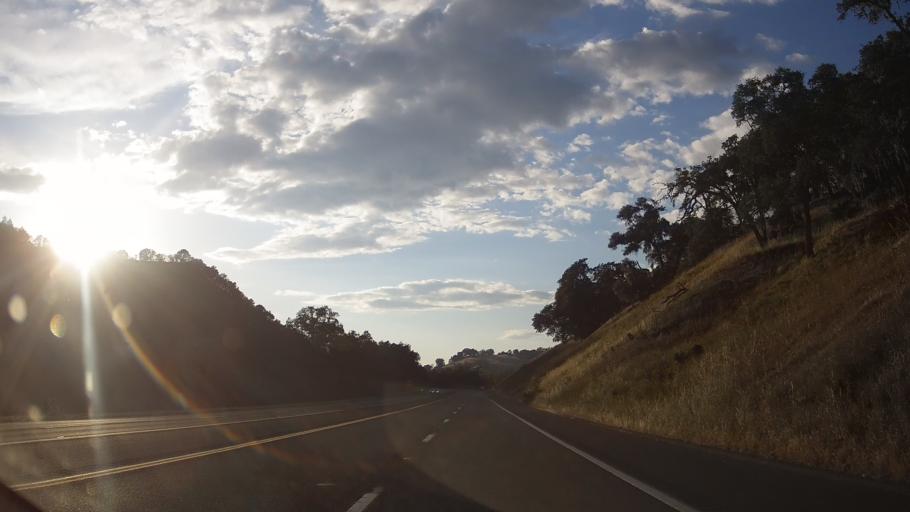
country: US
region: California
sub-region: Sonoma County
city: Cloverdale
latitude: 38.9302
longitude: -123.0587
